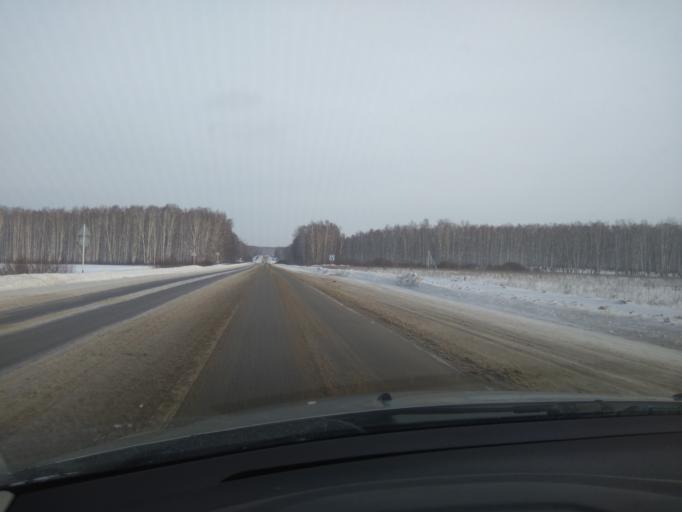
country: RU
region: Sverdlovsk
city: Bogdanovich
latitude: 56.7818
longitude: 61.9972
